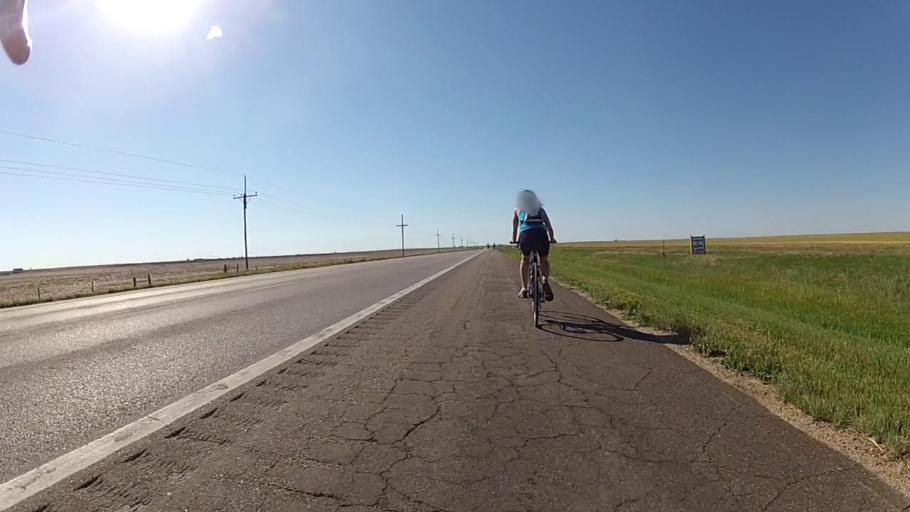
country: US
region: Kansas
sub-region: Ford County
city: Dodge City
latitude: 37.5941
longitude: -99.6930
